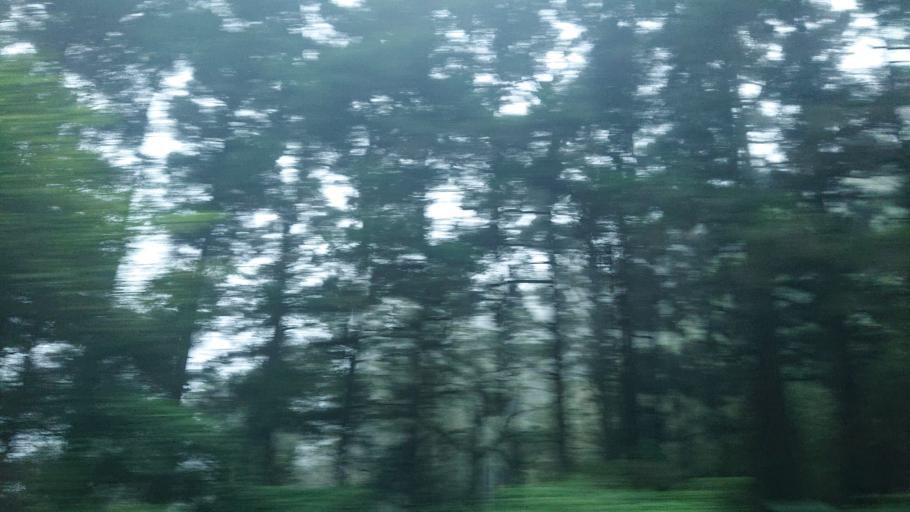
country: TW
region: Taiwan
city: Lugu
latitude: 23.5092
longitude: 120.7024
